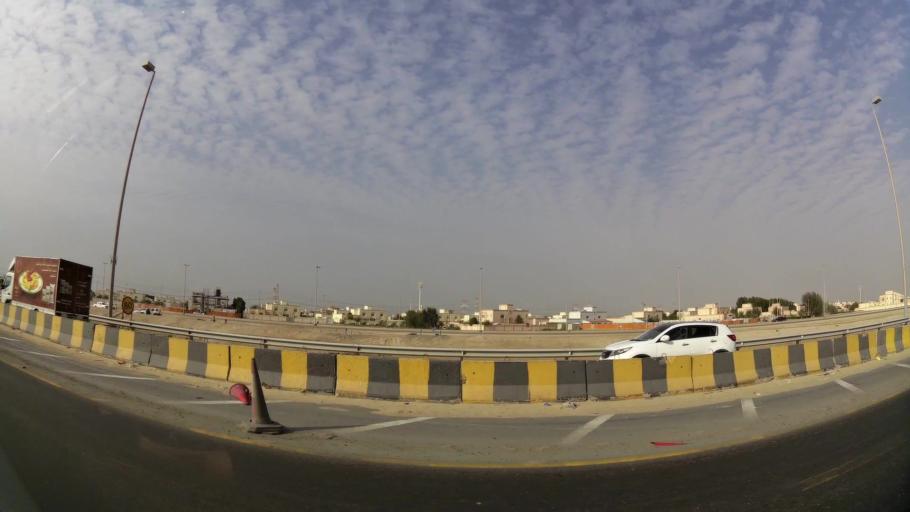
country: AE
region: Abu Dhabi
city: Abu Dhabi
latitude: 24.2929
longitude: 54.5542
